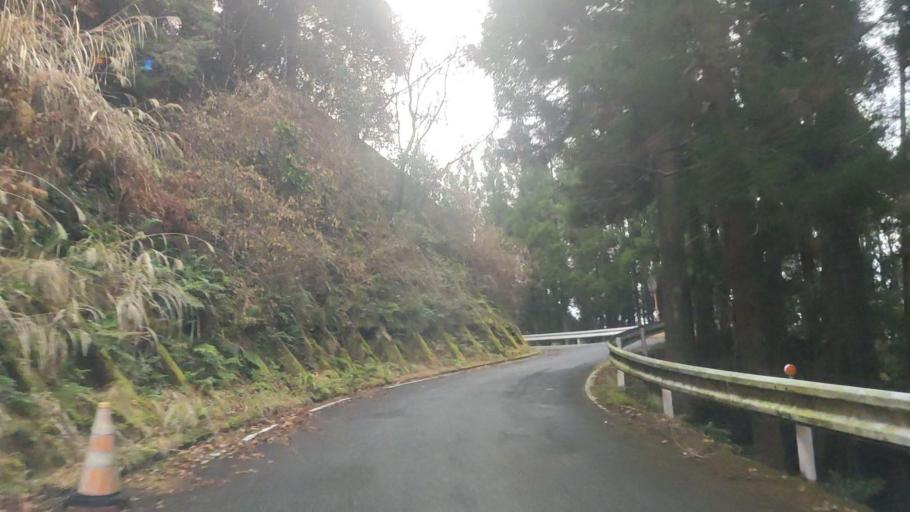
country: JP
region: Kumamoto
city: Matsubase
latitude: 32.5912
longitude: 130.8863
